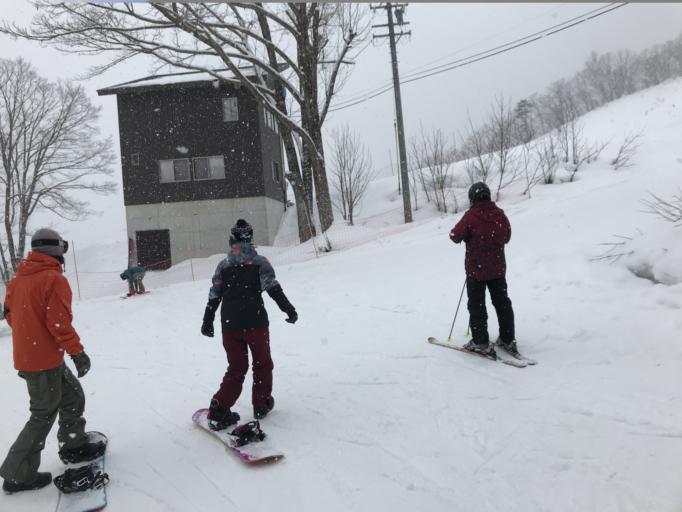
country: JP
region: Nagano
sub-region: Kitaazumi Gun
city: Hakuba
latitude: 36.7565
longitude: 137.8596
